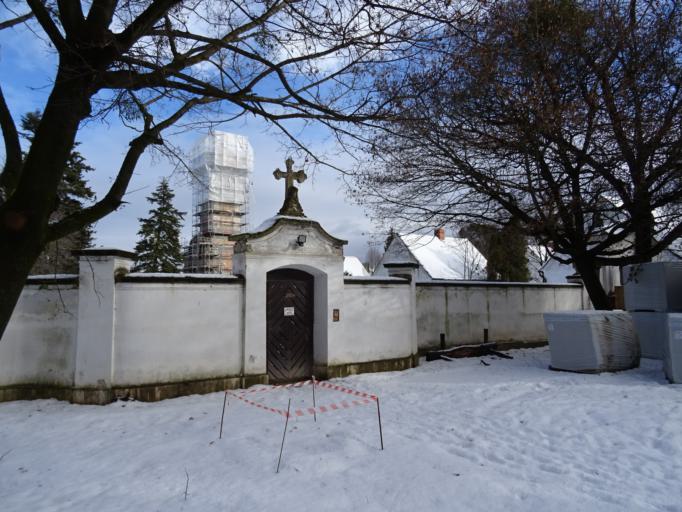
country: HU
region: Komarom-Esztergom
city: Oroszlany
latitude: 47.4966
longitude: 18.3369
